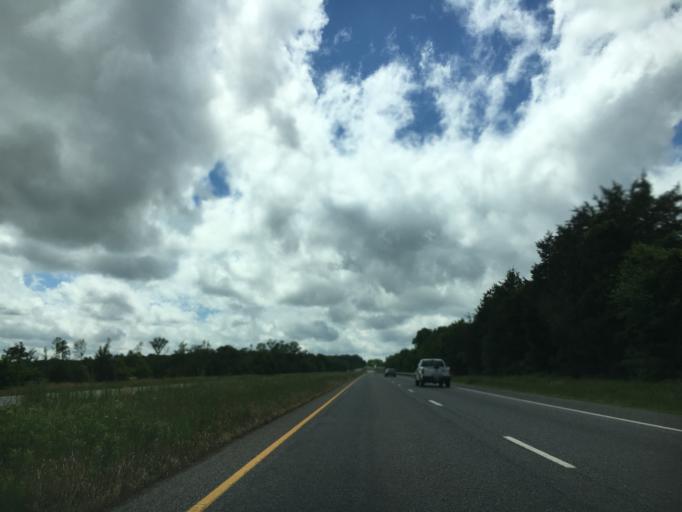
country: US
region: Virginia
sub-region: Mecklenburg County
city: Boydton
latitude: 36.6524
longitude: -78.4704
